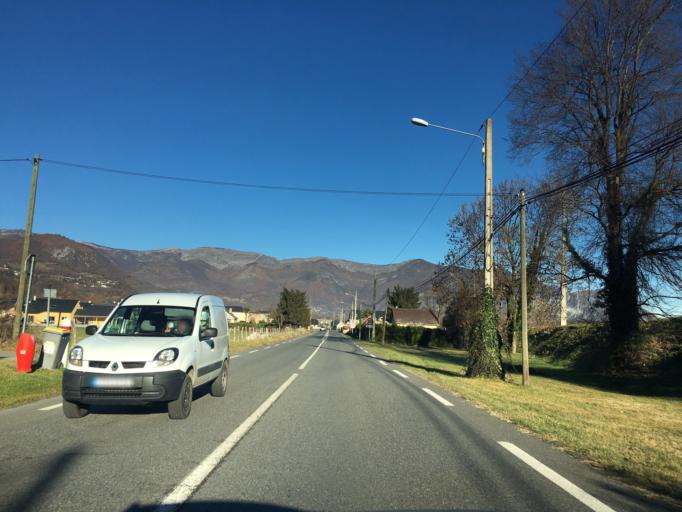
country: FR
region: Midi-Pyrenees
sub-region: Departement des Hautes-Pyrenees
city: Pierrefitte-Nestalas
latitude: 42.9715
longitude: -0.0750
